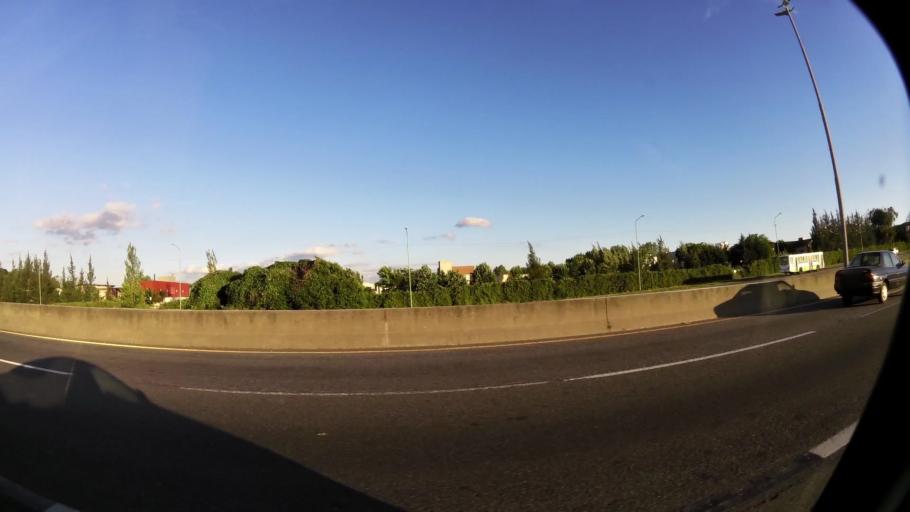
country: AR
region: Buenos Aires
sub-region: Partido de Quilmes
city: Quilmes
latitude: -34.7927
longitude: -58.1586
